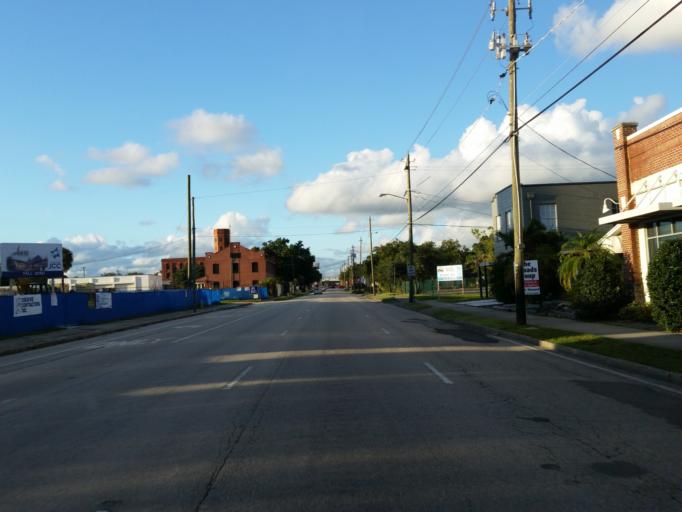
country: US
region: Florida
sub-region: Hillsborough County
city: Tampa
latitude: 27.9486
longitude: -82.4830
